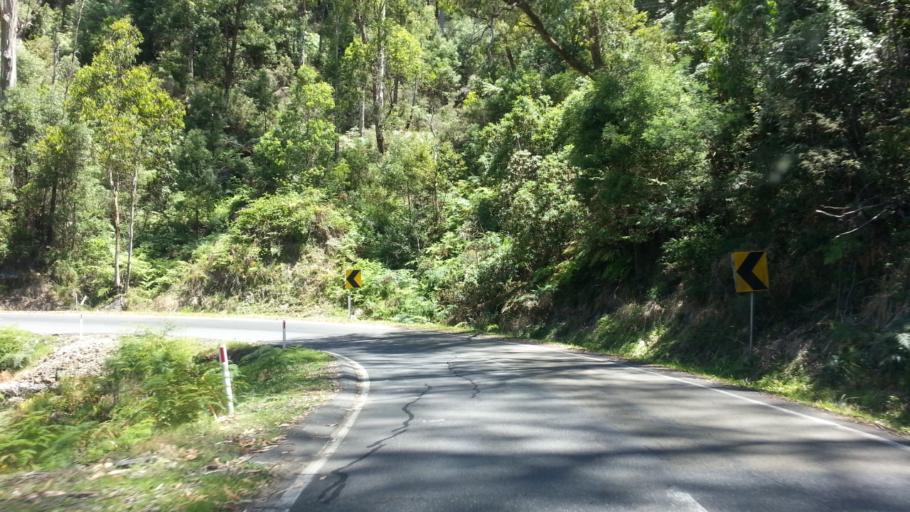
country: AU
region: Victoria
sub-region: Alpine
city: Mount Beauty
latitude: -36.7734
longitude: 147.2137
